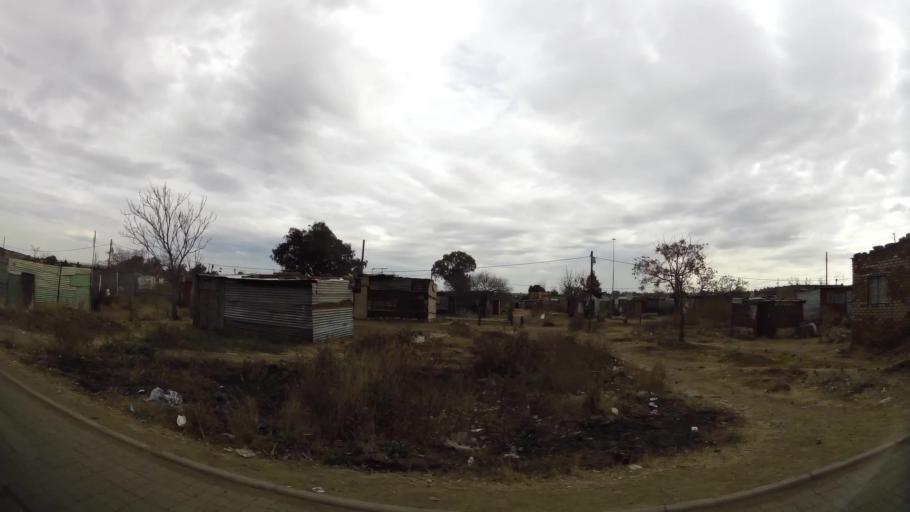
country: ZA
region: Orange Free State
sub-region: Fezile Dabi District Municipality
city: Kroonstad
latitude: -27.6498
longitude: 27.2208
